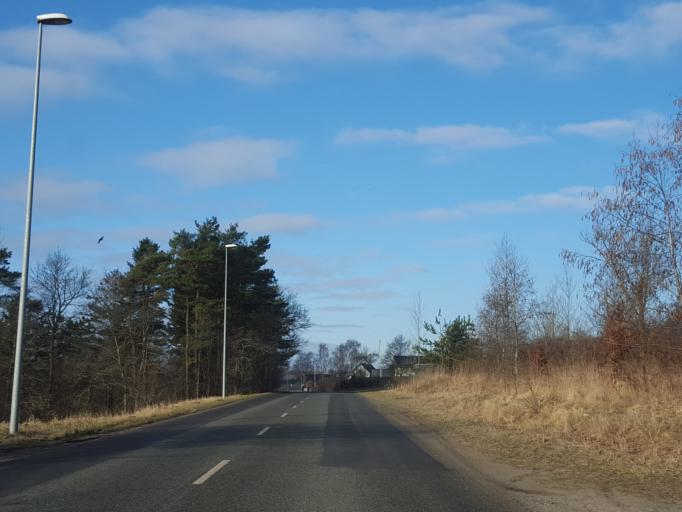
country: DK
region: North Denmark
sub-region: Alborg Kommune
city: Gistrup
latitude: 57.0023
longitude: 9.9515
